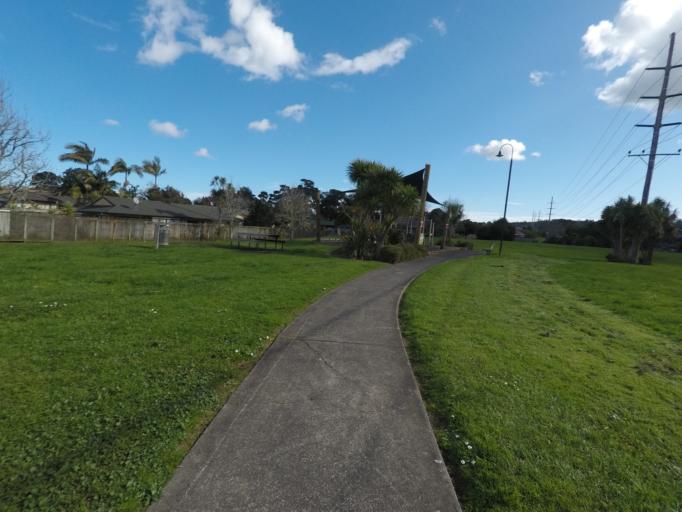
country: NZ
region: Auckland
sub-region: Auckland
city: Rothesay Bay
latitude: -36.7383
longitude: 174.6987
